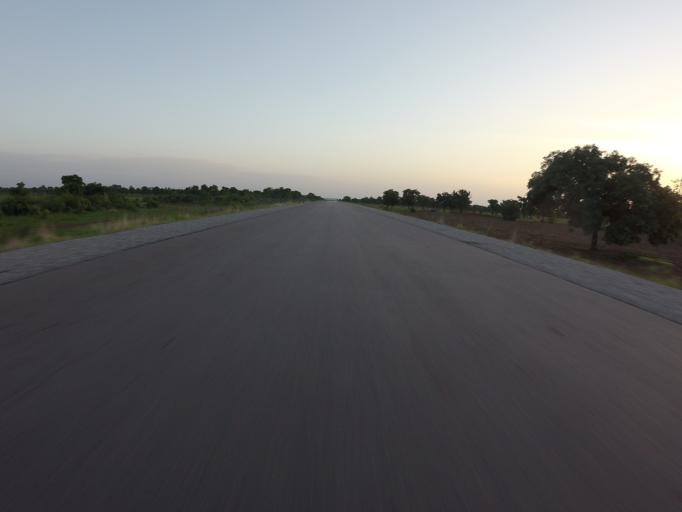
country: GH
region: Northern
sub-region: Yendi
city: Yendi
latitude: 9.9473
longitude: -0.1592
